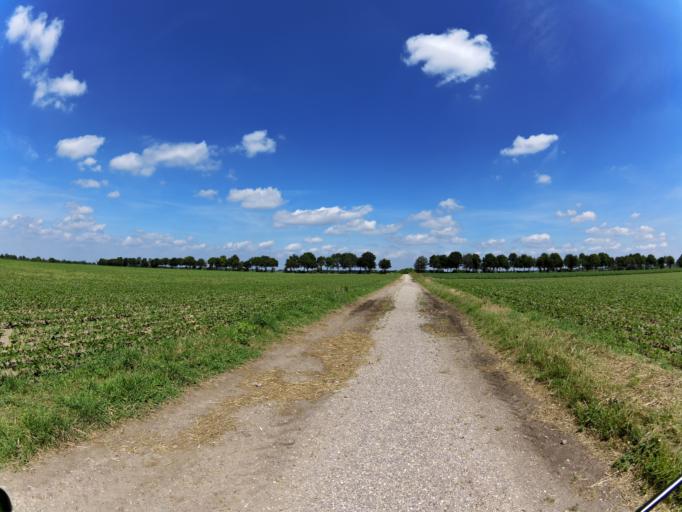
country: NL
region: Limburg
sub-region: Gemeente Sittard-Geleen
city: Sittard
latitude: 51.0180
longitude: 5.8925
